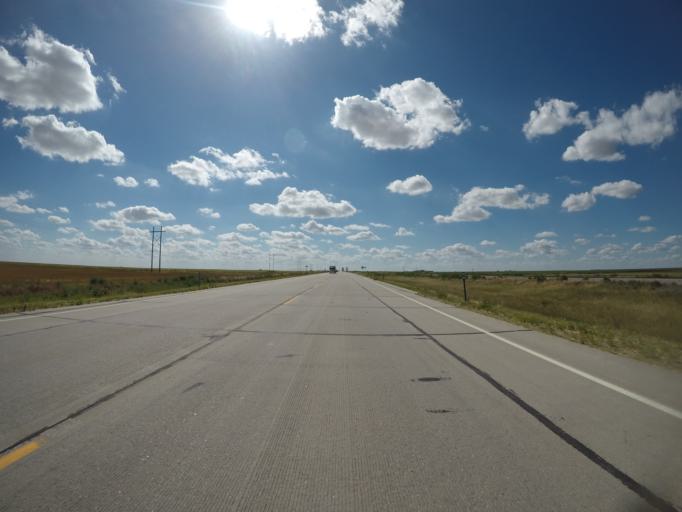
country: US
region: Colorado
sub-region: Phillips County
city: Holyoke
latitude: 40.6064
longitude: -102.4353
